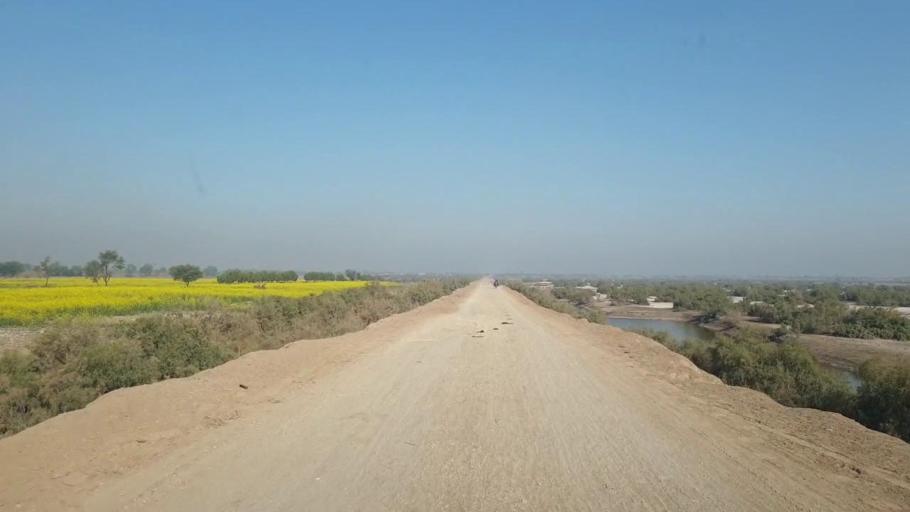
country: PK
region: Sindh
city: Shahdadpur
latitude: 25.9774
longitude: 68.4970
